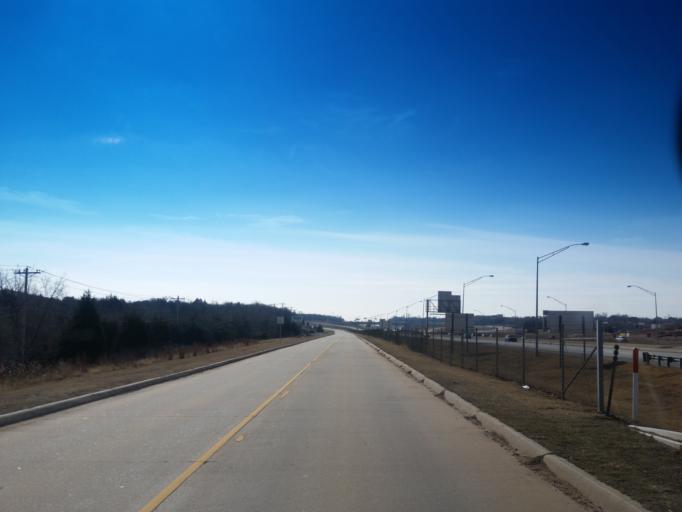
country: US
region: Oklahoma
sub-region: Oklahoma County
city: Edmond
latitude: 35.6467
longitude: -97.4243
